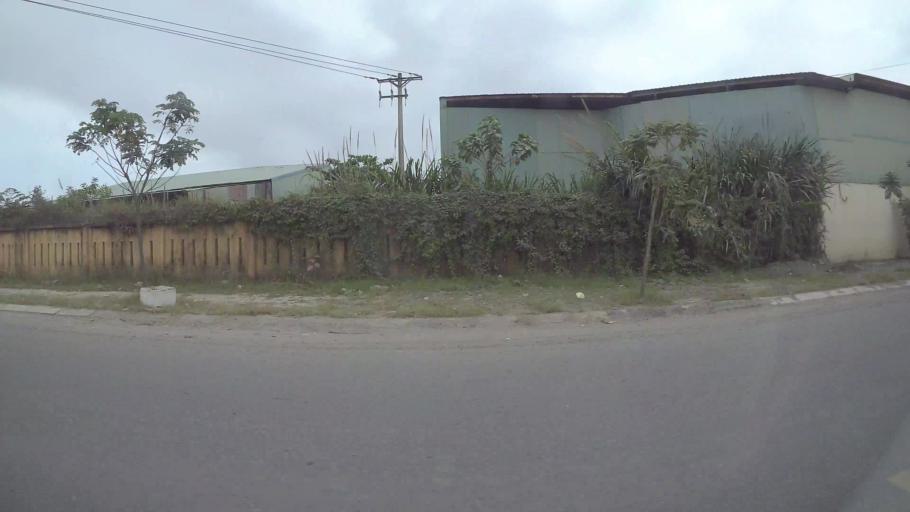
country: VN
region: Da Nang
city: Cam Le
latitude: 16.0376
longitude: 108.1729
